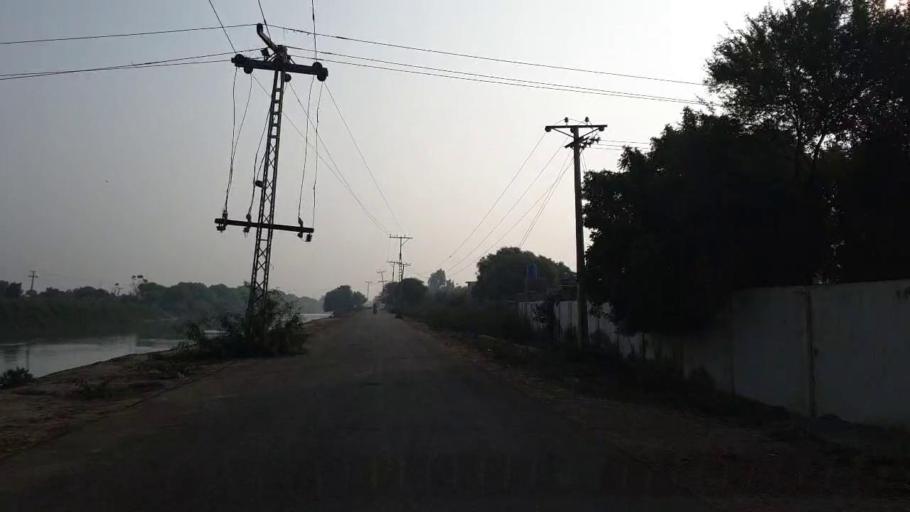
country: PK
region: Sindh
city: Tando Muhammad Khan
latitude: 25.1263
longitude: 68.5482
